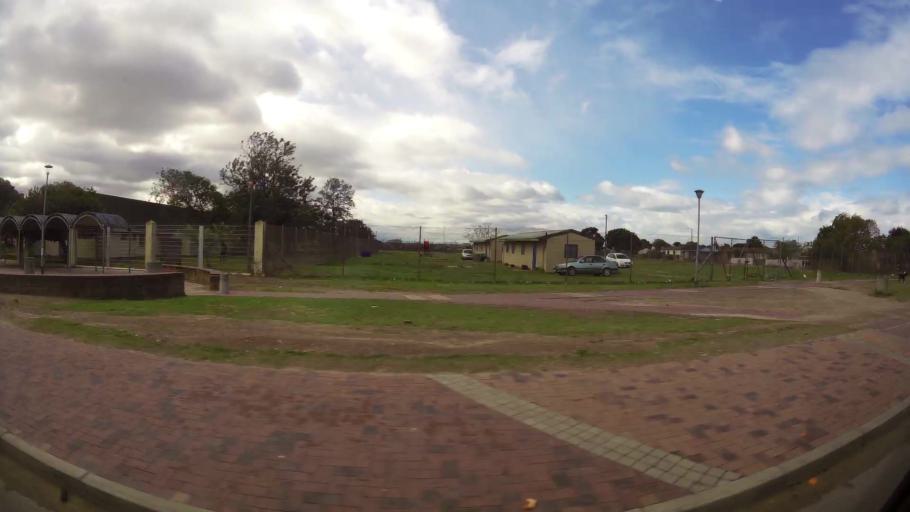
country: ZA
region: Western Cape
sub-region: Eden District Municipality
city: George
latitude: -33.9843
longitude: 22.4728
